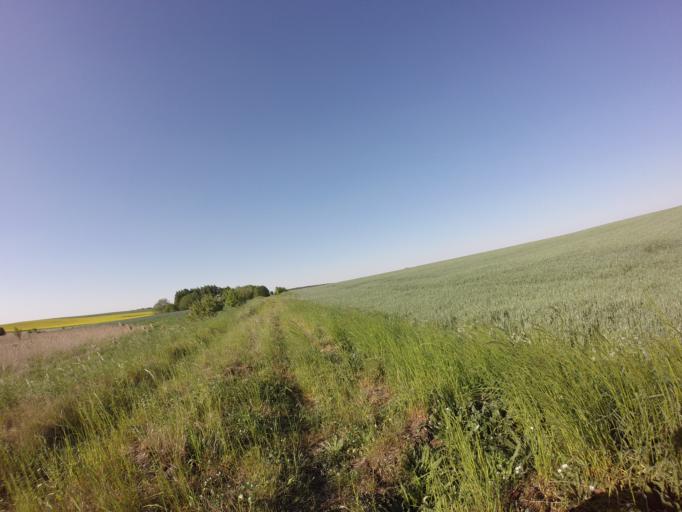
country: PL
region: West Pomeranian Voivodeship
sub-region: Powiat choszczenski
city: Choszczno
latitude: 53.1432
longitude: 15.3702
